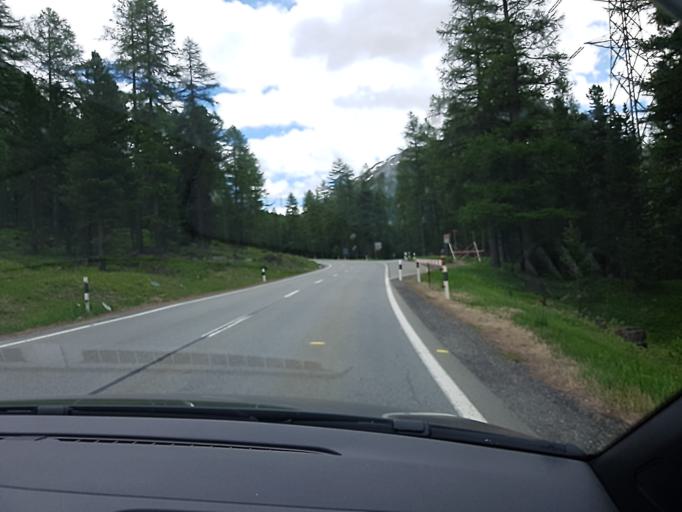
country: CH
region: Grisons
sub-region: Maloja District
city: Pontresina
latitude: 46.4635
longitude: 9.9347
